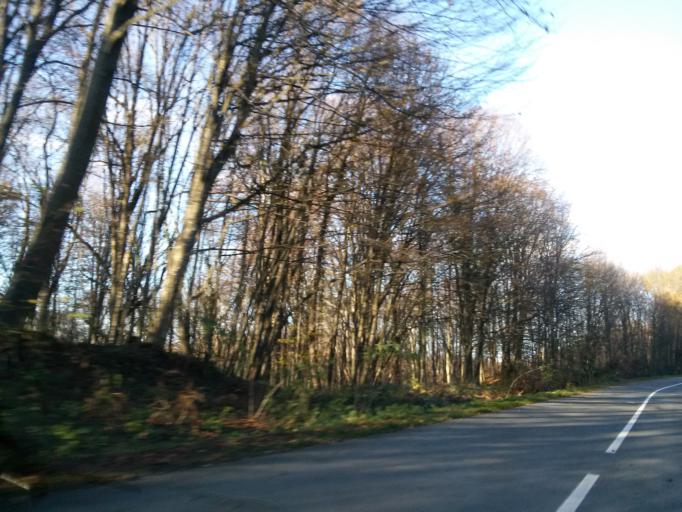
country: HR
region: Sisacko-Moslavacka
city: Gvozd
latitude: 45.3764
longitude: 15.9129
